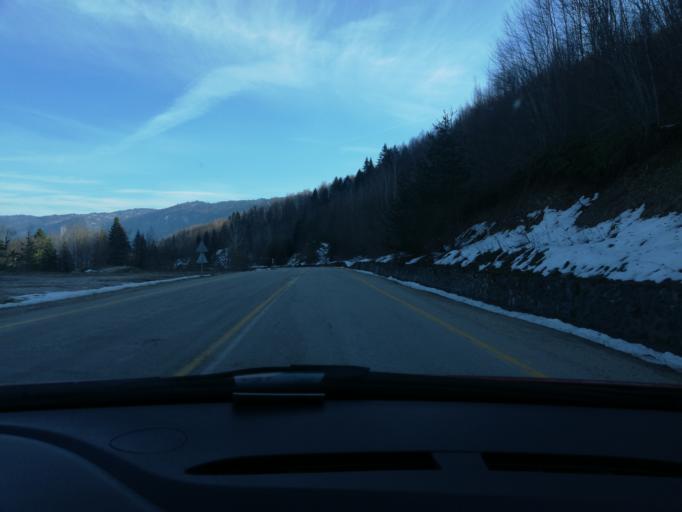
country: TR
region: Kastamonu
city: Senpazar
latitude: 41.7903
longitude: 33.1337
